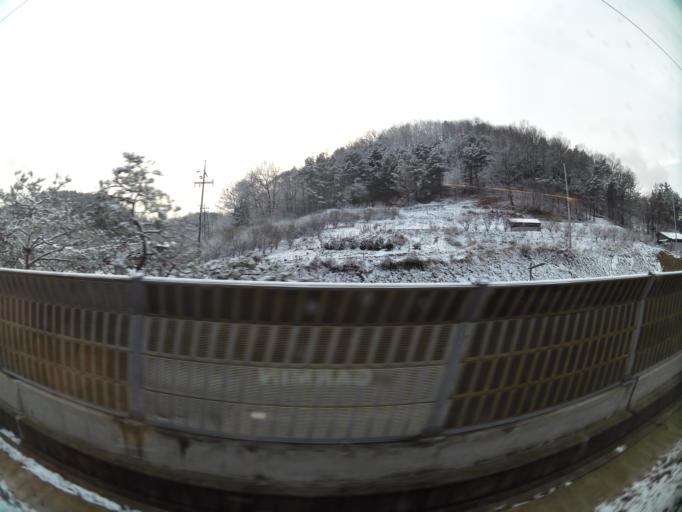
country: KR
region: Daejeon
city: Daejeon
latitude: 36.3164
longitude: 127.4528
